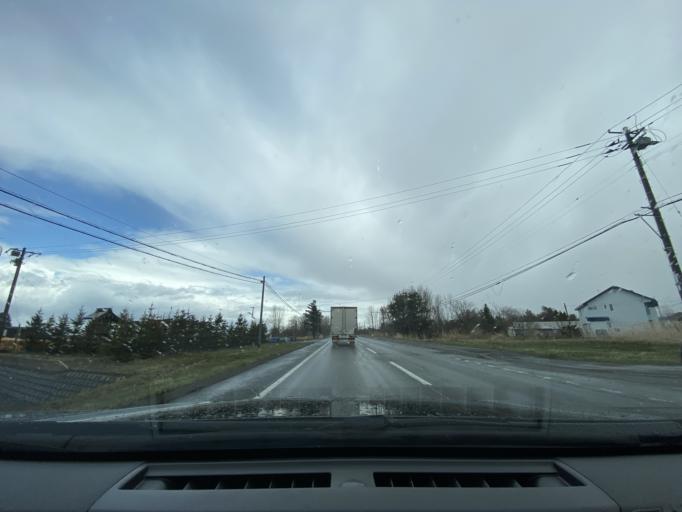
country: JP
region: Hokkaido
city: Fukagawa
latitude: 43.6848
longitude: 142.0465
